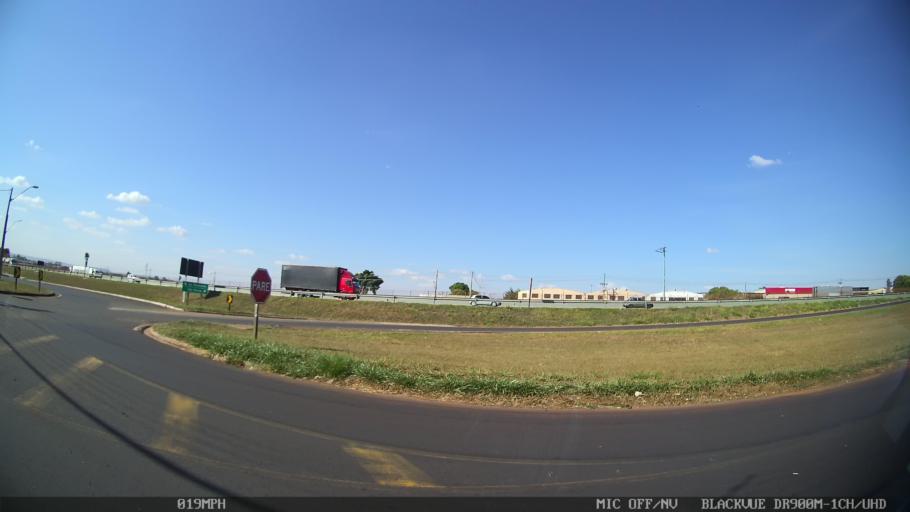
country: BR
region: Sao Paulo
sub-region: Ribeirao Preto
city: Ribeirao Preto
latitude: -21.1805
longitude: -47.7576
